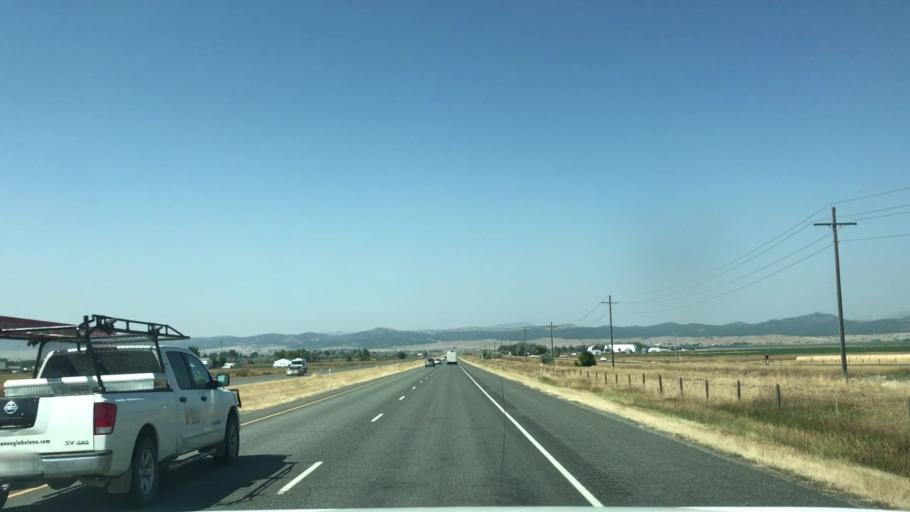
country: US
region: Montana
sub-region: Lewis and Clark County
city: Helena Valley West Central
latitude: 46.6725
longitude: -112.0114
